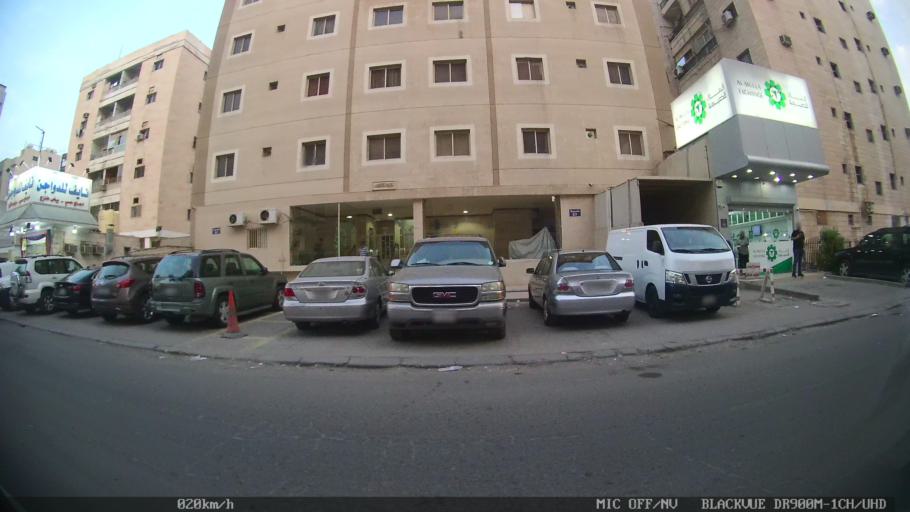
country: KW
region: Al Farwaniyah
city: Al Farwaniyah
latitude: 29.2874
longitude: 47.9701
